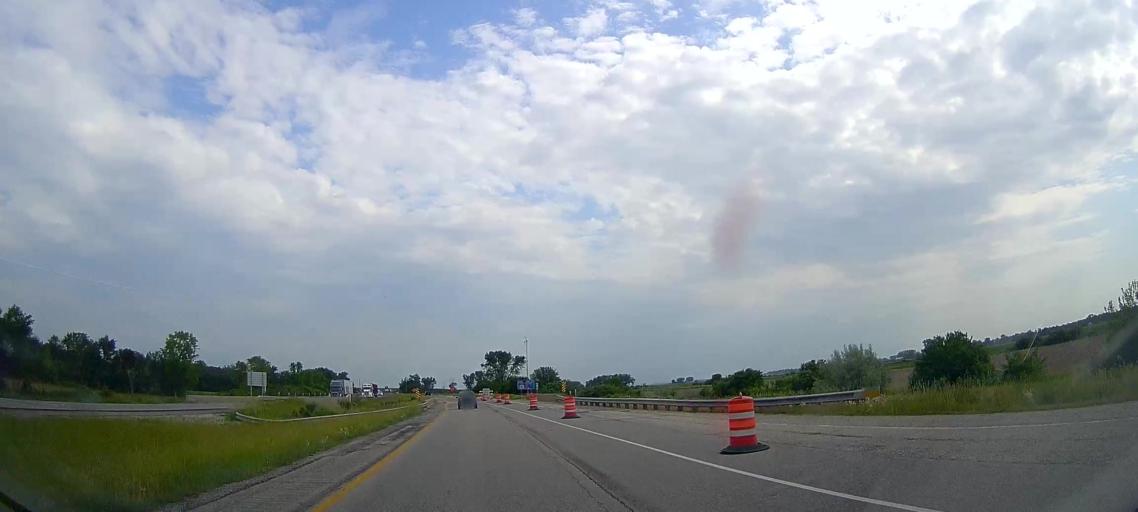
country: US
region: Nebraska
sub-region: Burt County
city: Tekamah
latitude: 41.7365
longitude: -96.0484
